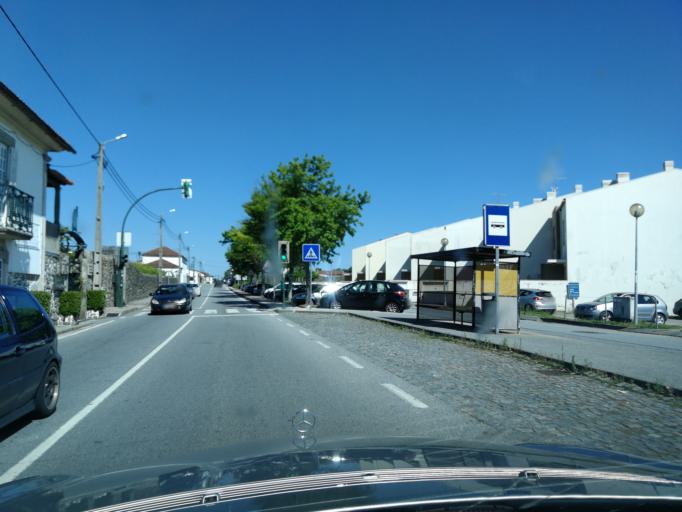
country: PT
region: Viana do Castelo
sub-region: Viana do Castelo
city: Meadela
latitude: 41.7093
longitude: -8.7724
